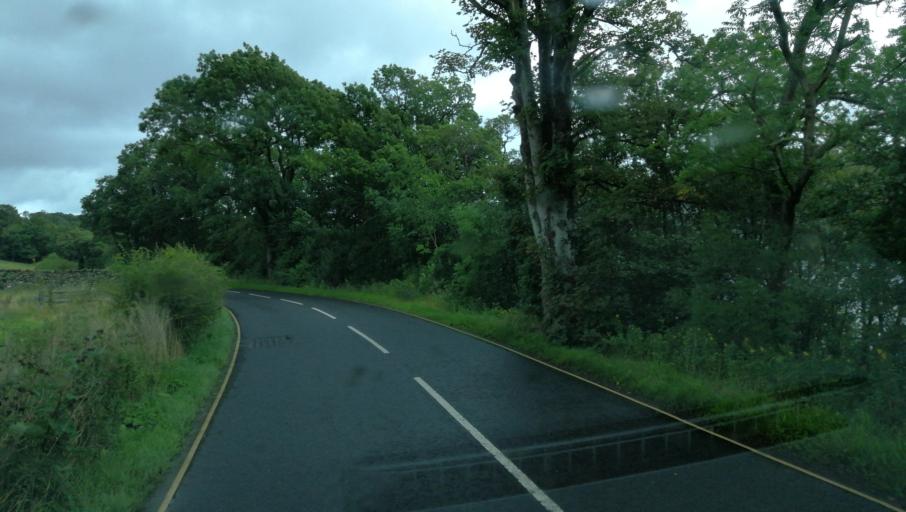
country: GB
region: England
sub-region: Cumbria
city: Penrith
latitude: 54.5800
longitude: -2.8815
